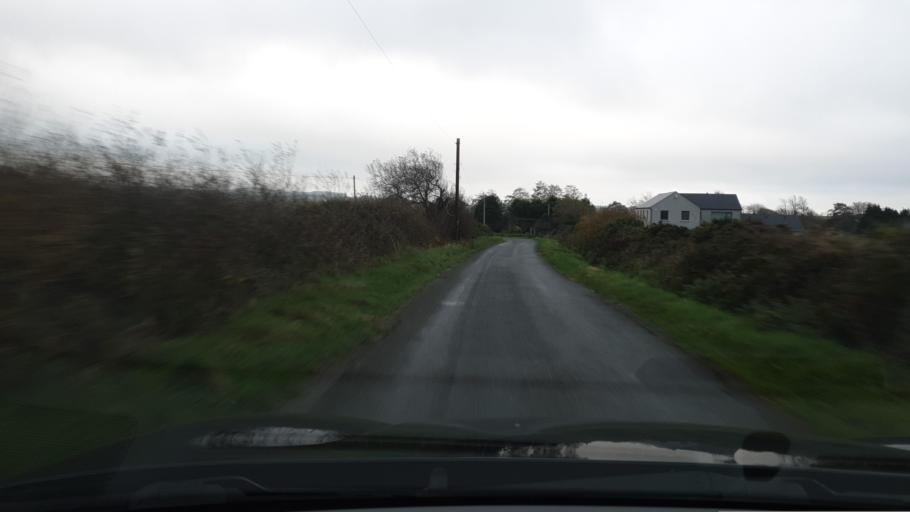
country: IE
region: Leinster
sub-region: Wicklow
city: Kilmacanoge
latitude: 53.1197
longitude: -6.1917
